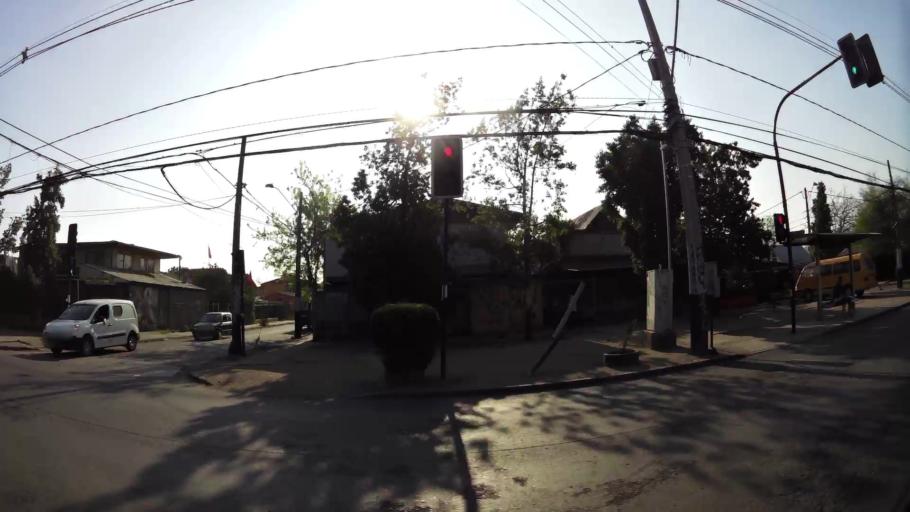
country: CL
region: Santiago Metropolitan
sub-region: Provincia de Santiago
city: Santiago
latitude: -33.3859
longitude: -70.6416
